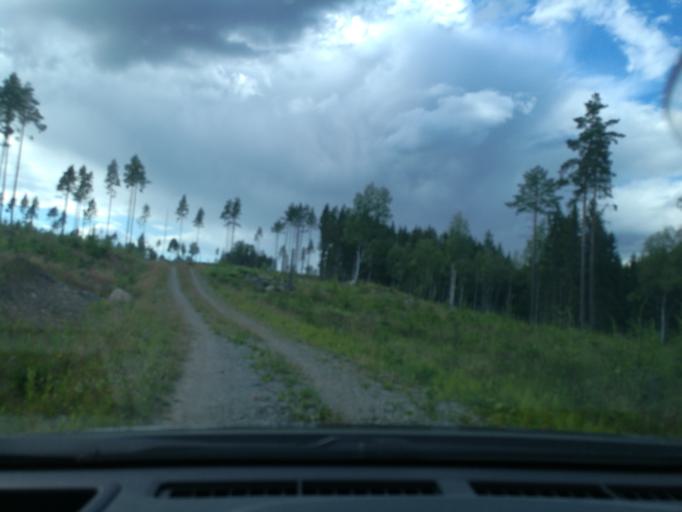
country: SE
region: Vaestmanland
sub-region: Surahammars Kommun
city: Ramnas
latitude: 59.8021
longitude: 16.2914
